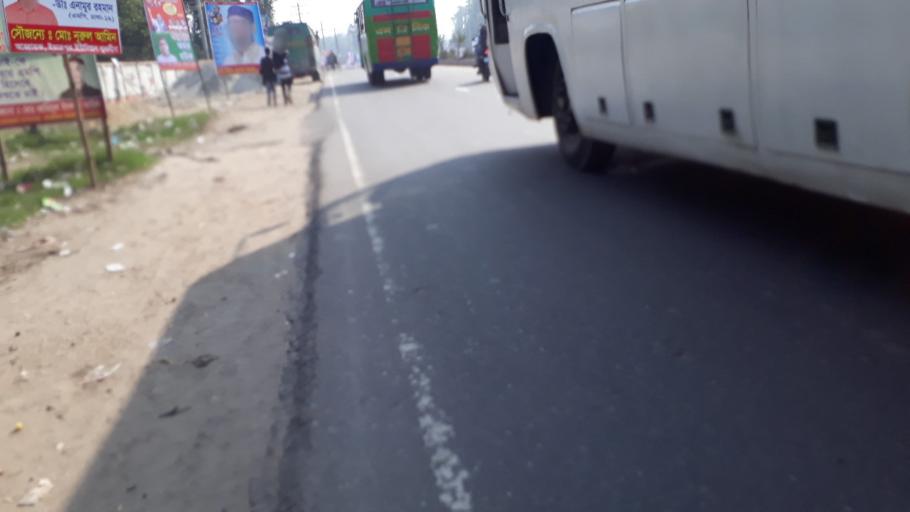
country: BD
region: Dhaka
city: Tungi
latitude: 23.8948
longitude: 90.2714
